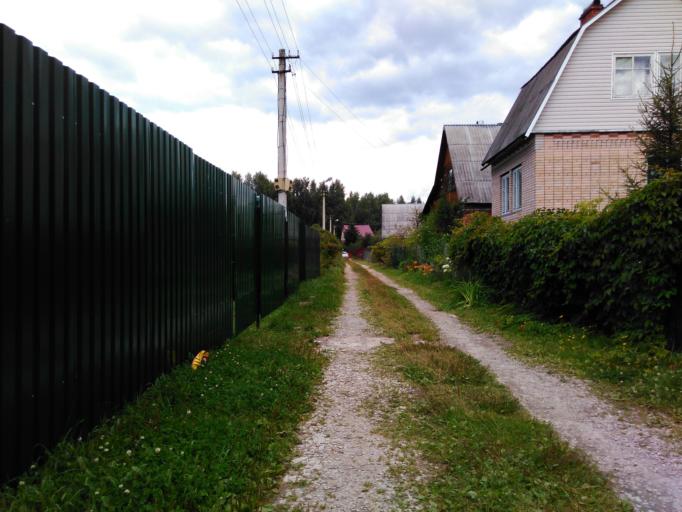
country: RU
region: Vladimir
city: Pokrov
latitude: 55.8766
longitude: 39.1252
